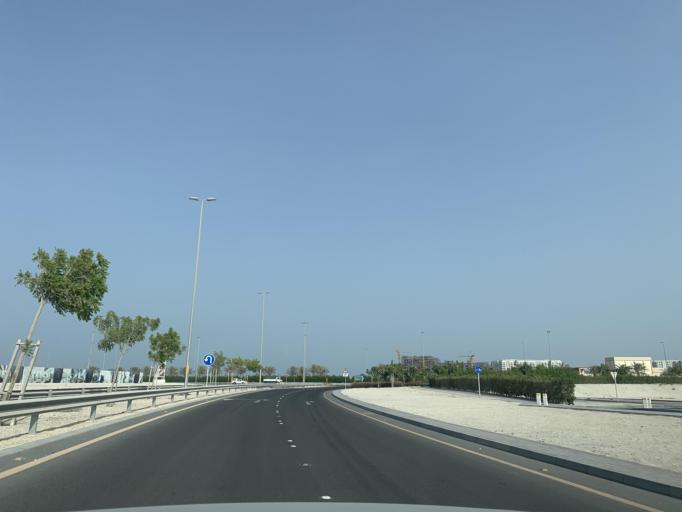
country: BH
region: Muharraq
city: Al Muharraq
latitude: 26.3125
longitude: 50.6401
